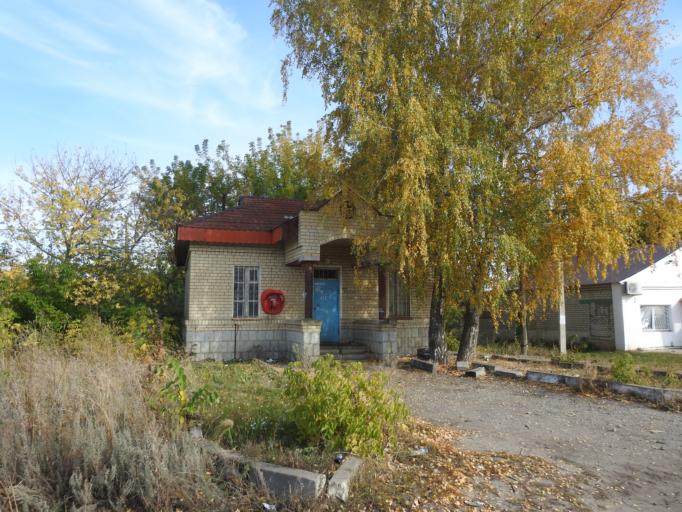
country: RU
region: Saratov
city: Baltay
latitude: 52.5062
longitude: 46.8028
